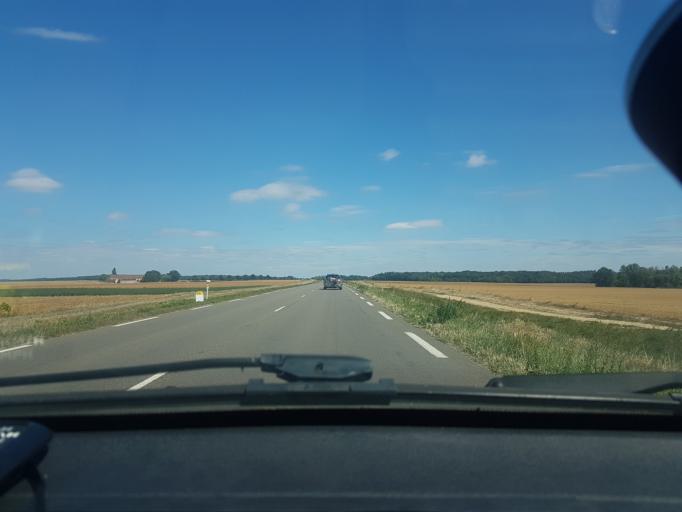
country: FR
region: Bourgogne
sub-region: Departement de la Cote-d'Or
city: Arc-sur-Tille
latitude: 47.3507
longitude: 5.2032
